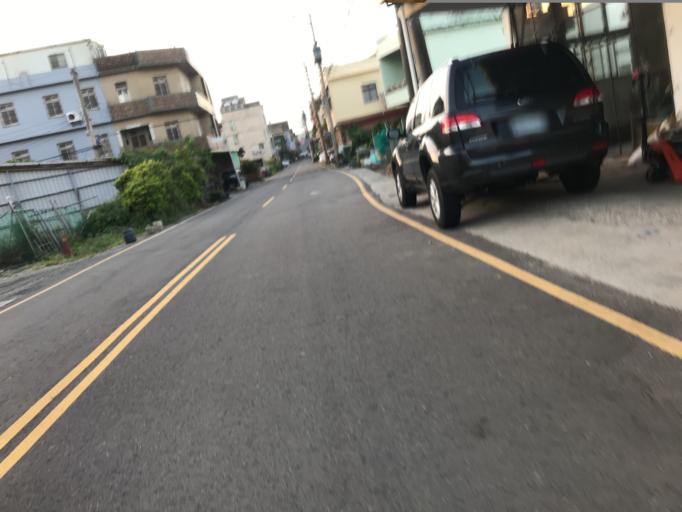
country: TW
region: Taiwan
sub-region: Hsinchu
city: Hsinchu
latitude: 24.8036
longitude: 120.9391
